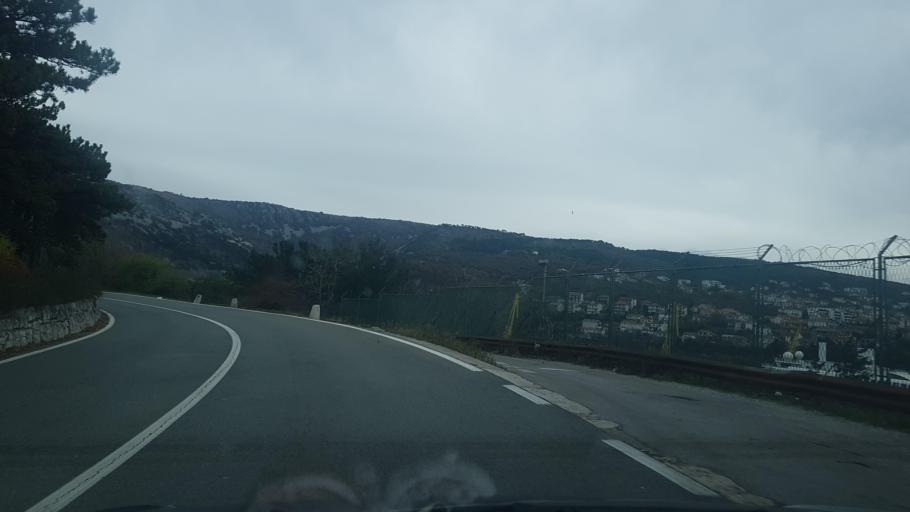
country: HR
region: Primorsko-Goranska
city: Cavle
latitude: 45.3136
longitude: 14.4759
